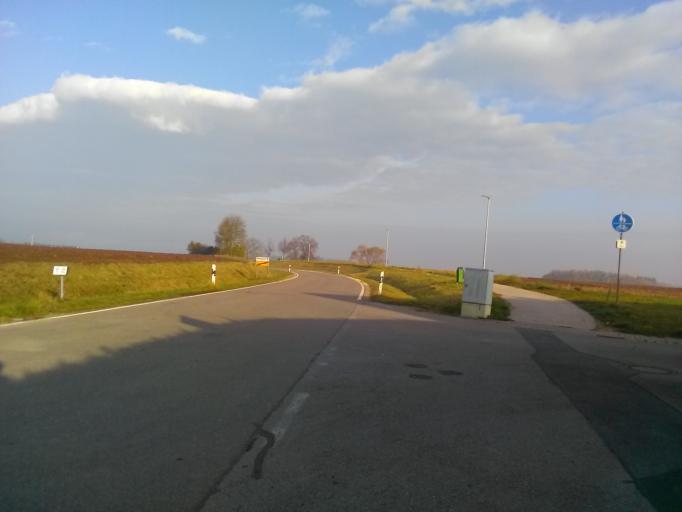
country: DE
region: Bavaria
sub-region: Regierungsbezirk Mittelfranken
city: Bruckberg
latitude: 49.3147
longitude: 10.7090
